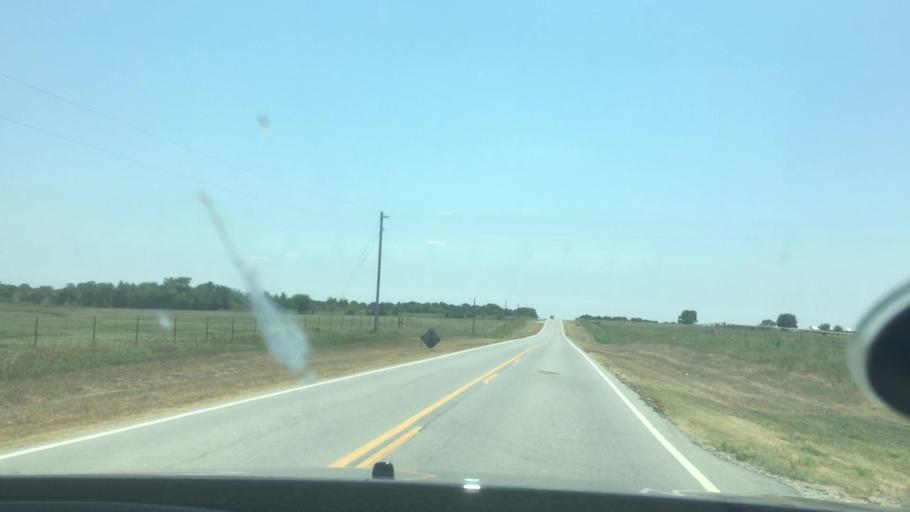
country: US
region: Oklahoma
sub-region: Coal County
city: Coalgate
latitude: 34.5671
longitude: -96.4069
